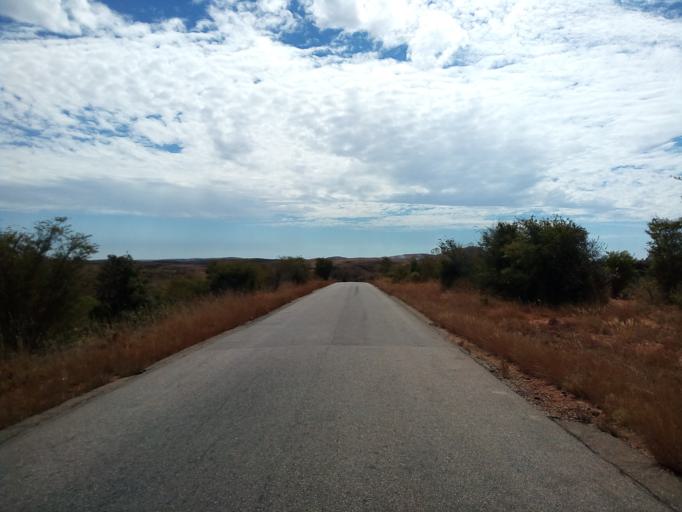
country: MG
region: Betsiboka
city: Maevatanana
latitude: -17.2478
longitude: 46.9266
